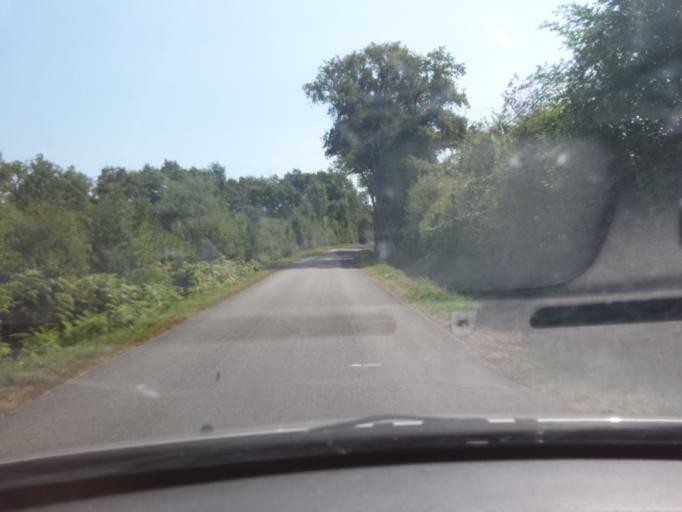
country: FR
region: Poitou-Charentes
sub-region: Departement de la Vienne
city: Availles-Limouzine
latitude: 46.1079
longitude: 0.6935
